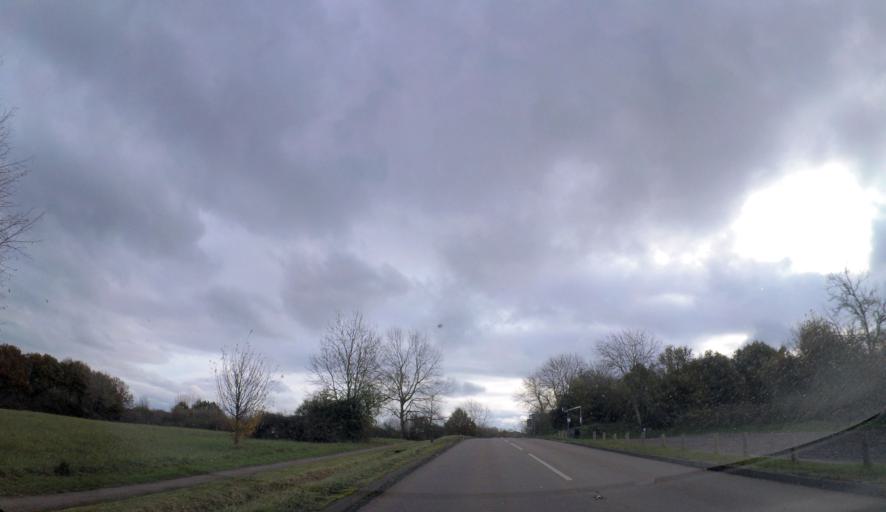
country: GB
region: England
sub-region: Surrey
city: Salfords
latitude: 51.2120
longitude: -0.1740
